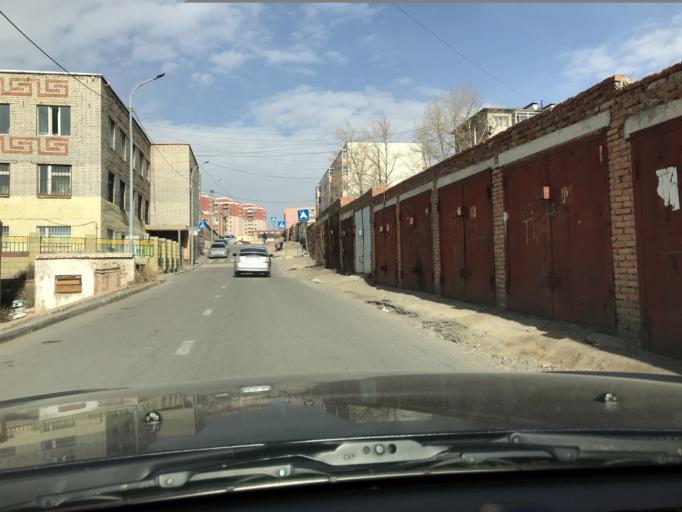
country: MN
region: Ulaanbaatar
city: Ulaanbaatar
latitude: 47.9236
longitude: 106.9452
